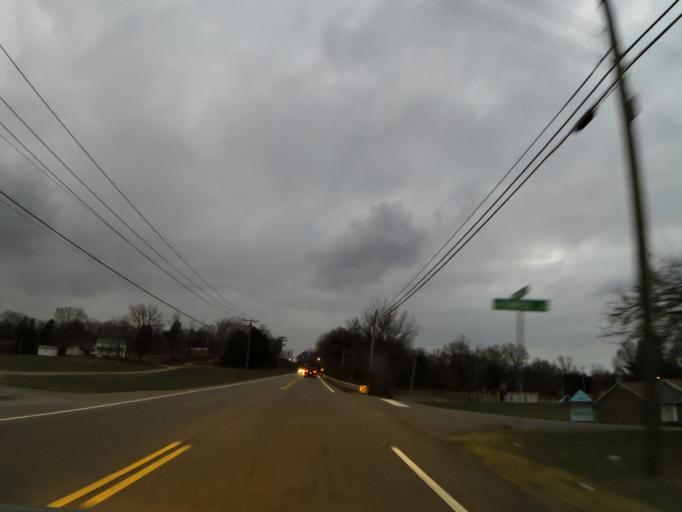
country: US
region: Tennessee
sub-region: Knox County
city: Knoxville
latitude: 35.8797
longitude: -83.9384
